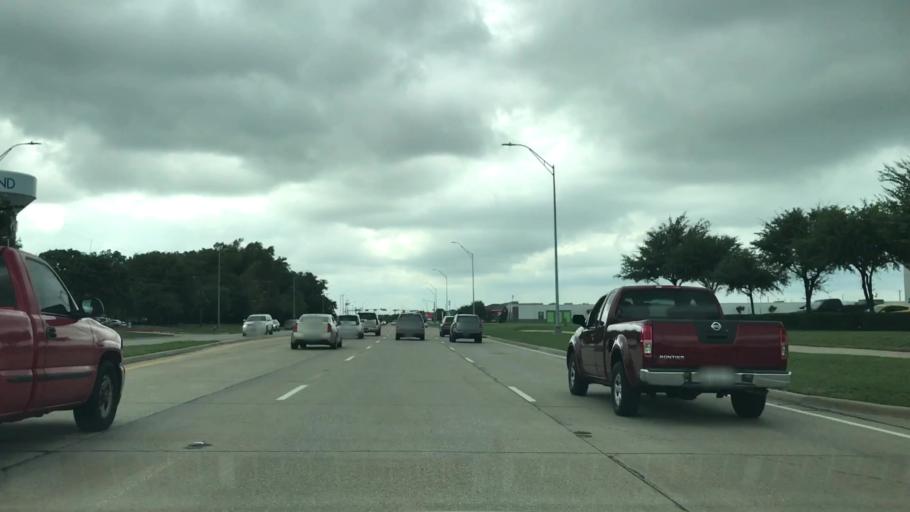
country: US
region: Texas
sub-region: Dallas County
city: Garland
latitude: 32.9108
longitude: -96.6079
